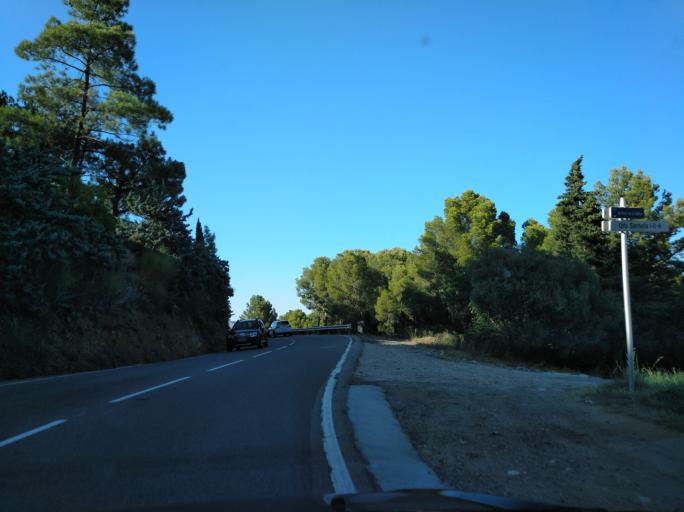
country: ES
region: Catalonia
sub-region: Provincia de Girona
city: Llanca
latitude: 42.3529
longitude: 3.1747
